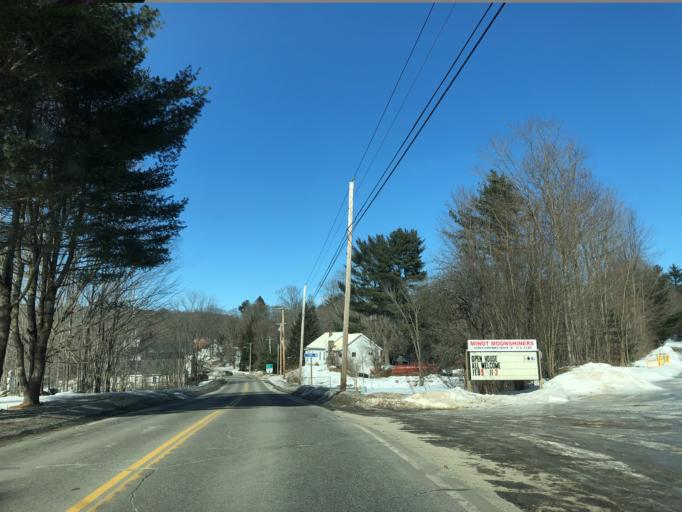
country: US
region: Maine
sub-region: Oxford County
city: Hebron
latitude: 44.1696
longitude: -70.3656
